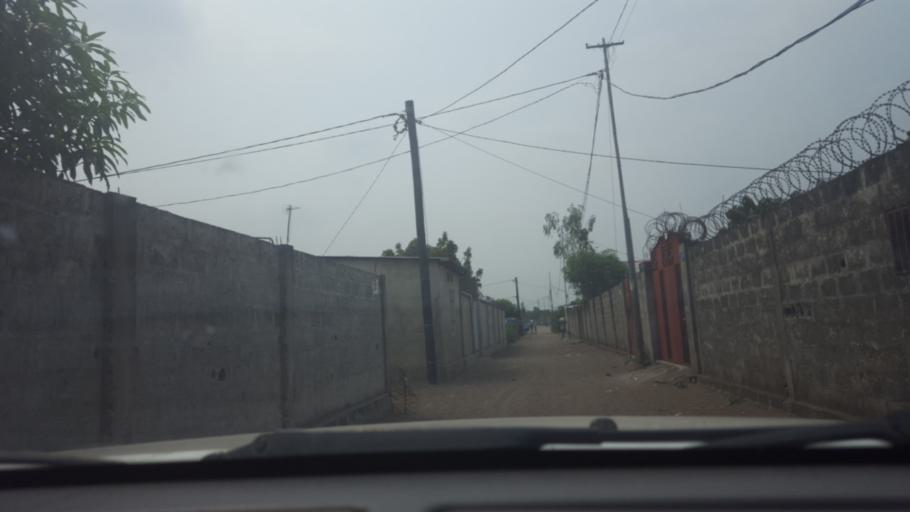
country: CD
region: Kinshasa
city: Masina
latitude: -4.3550
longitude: 15.5083
